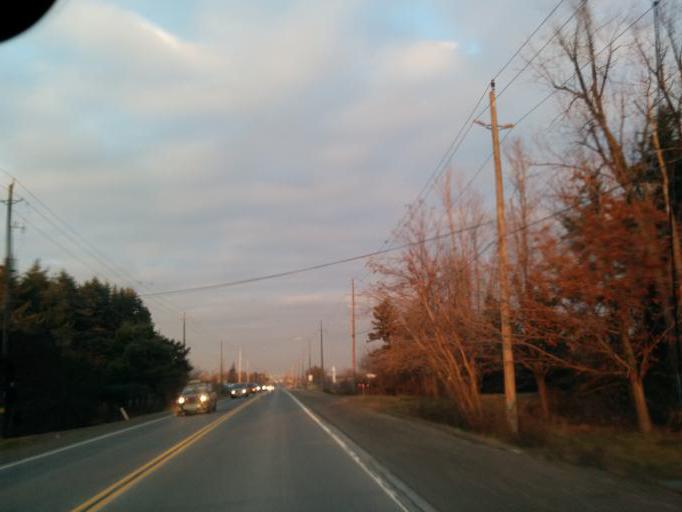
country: CA
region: Ontario
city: Brampton
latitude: 43.8245
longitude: -79.7219
